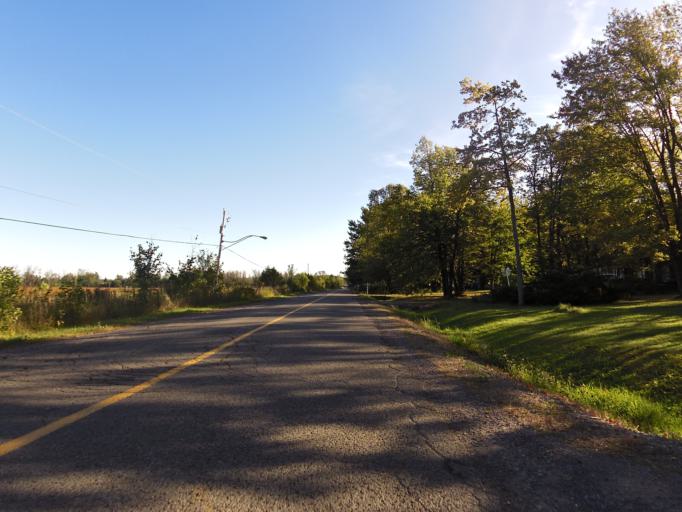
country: CA
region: Ontario
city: Bells Corners
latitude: 45.4641
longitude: -75.8846
